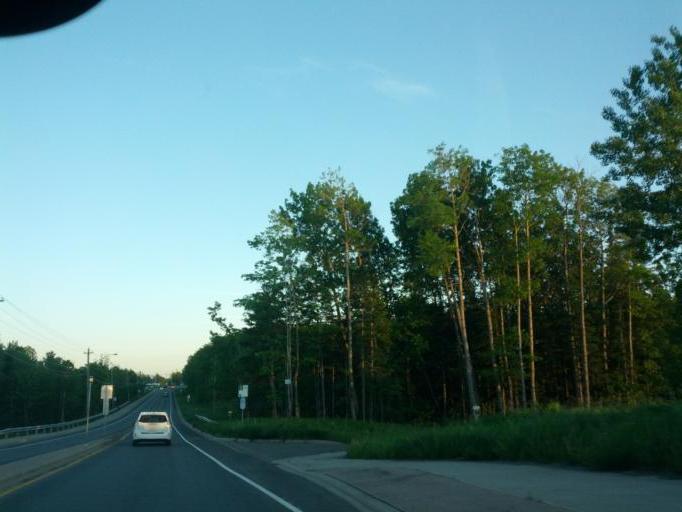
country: CA
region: New Brunswick
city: Moncton
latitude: 46.1034
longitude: -64.8623
